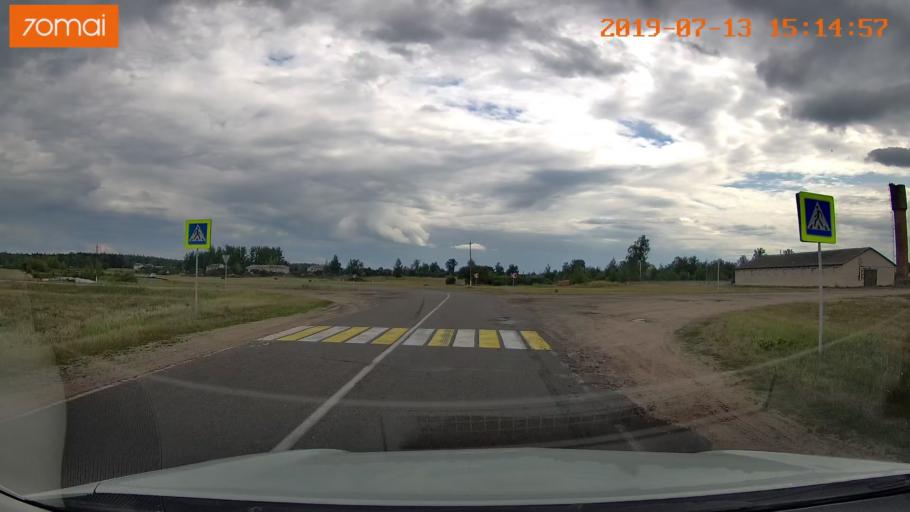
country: BY
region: Mogilev
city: Hlusha
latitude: 53.1203
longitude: 28.8214
